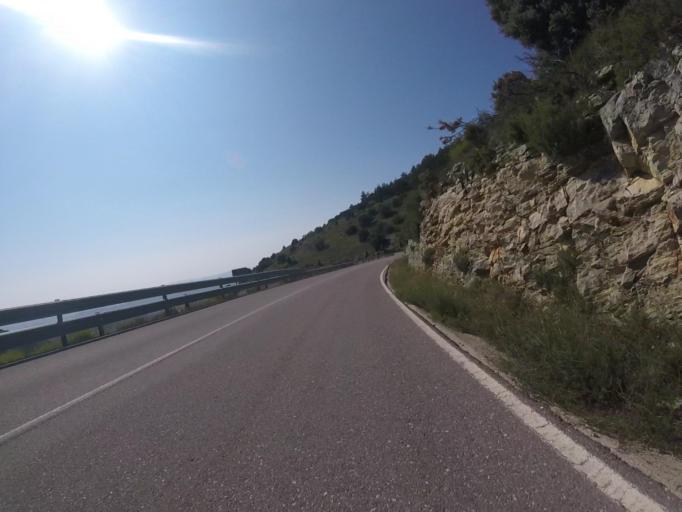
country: ES
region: Valencia
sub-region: Provincia de Castello
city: Benafigos
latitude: 40.2667
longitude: -0.2345
